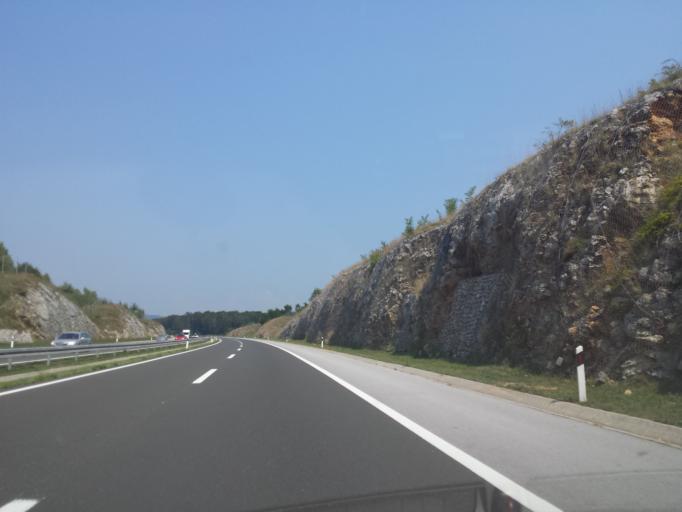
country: HR
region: Karlovacka
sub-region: Grad Ogulin
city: Ogulin
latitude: 45.3518
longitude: 15.2780
